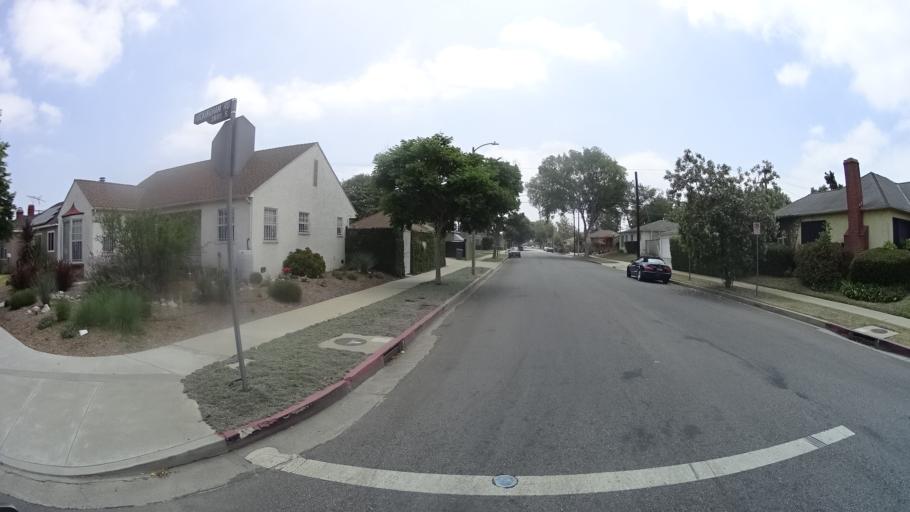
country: US
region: California
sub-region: Los Angeles County
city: View Park-Windsor Hills
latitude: 34.0161
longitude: -118.3407
